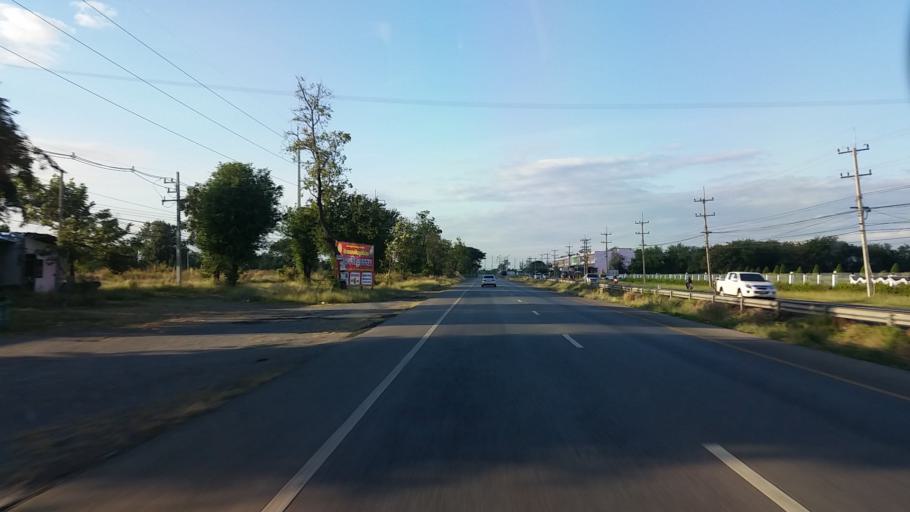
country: TH
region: Lop Buri
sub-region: Amphoe Tha Luang
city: Tha Luang
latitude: 15.0952
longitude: 101.0162
